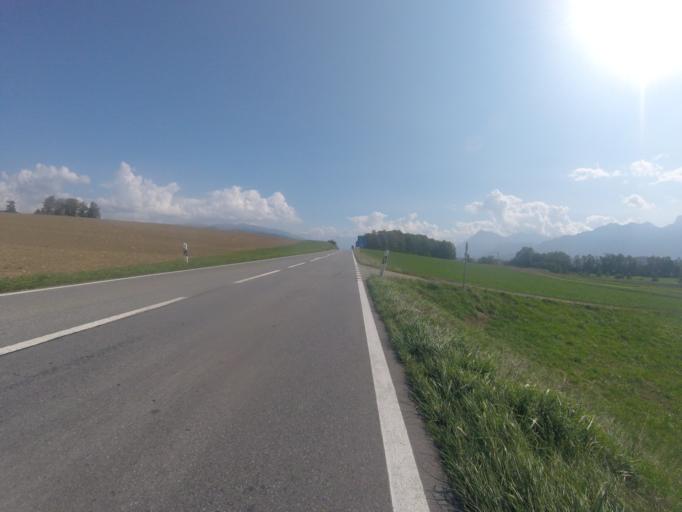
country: CH
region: Bern
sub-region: Thun District
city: Uttigen
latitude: 46.7886
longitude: 7.5696
